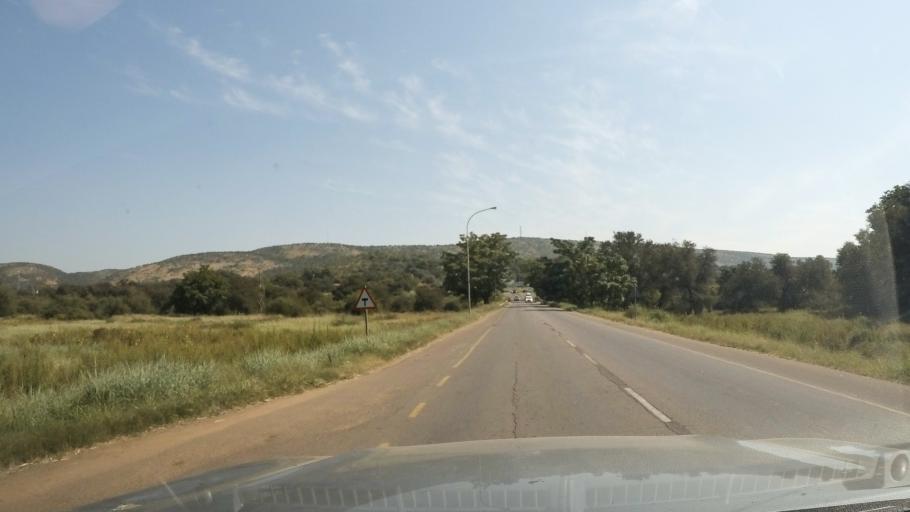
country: BW
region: South East
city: Lobatse
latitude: -25.2272
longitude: 25.6794
